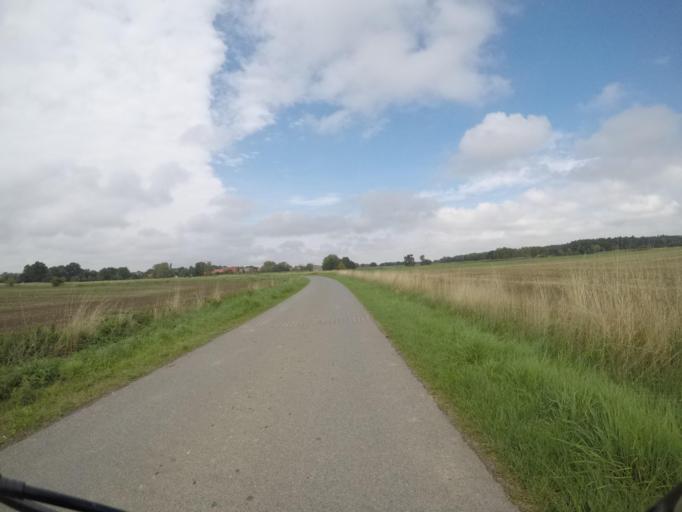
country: DE
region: Lower Saxony
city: Neu Darchau
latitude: 53.3011
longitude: 10.8960
